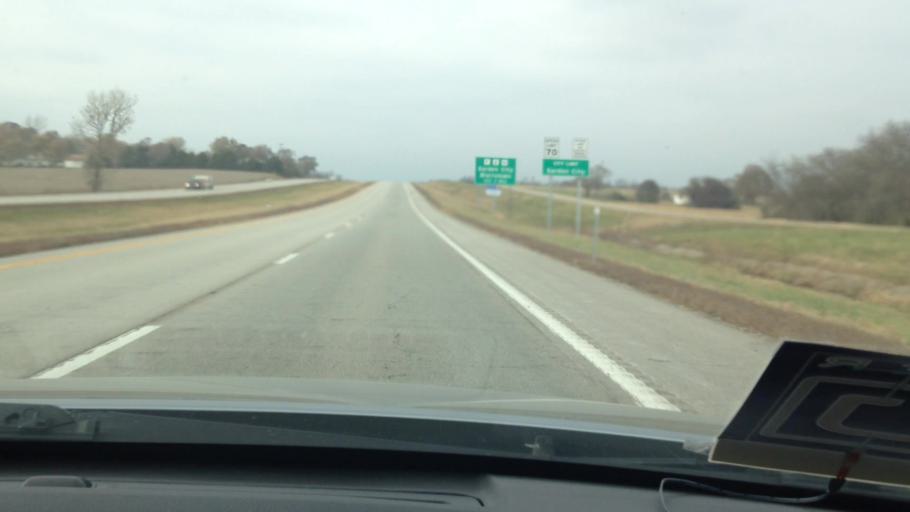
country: US
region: Missouri
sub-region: Cass County
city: Garden City
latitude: 38.5591
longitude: -94.1814
